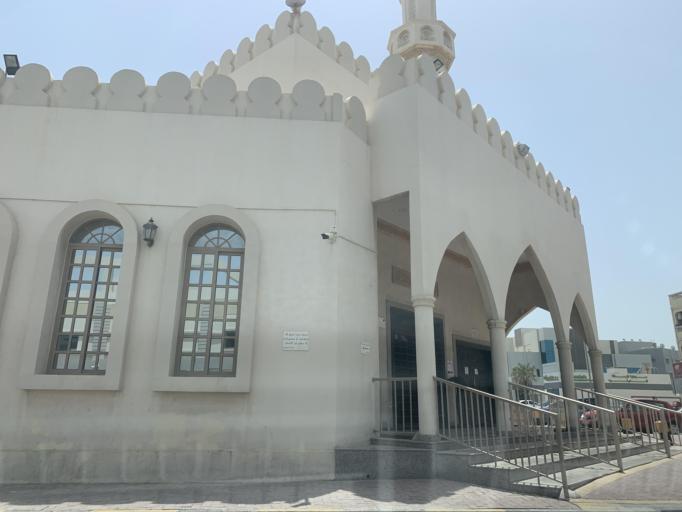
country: BH
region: Northern
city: Madinat `Isa
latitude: 26.1677
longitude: 50.5639
